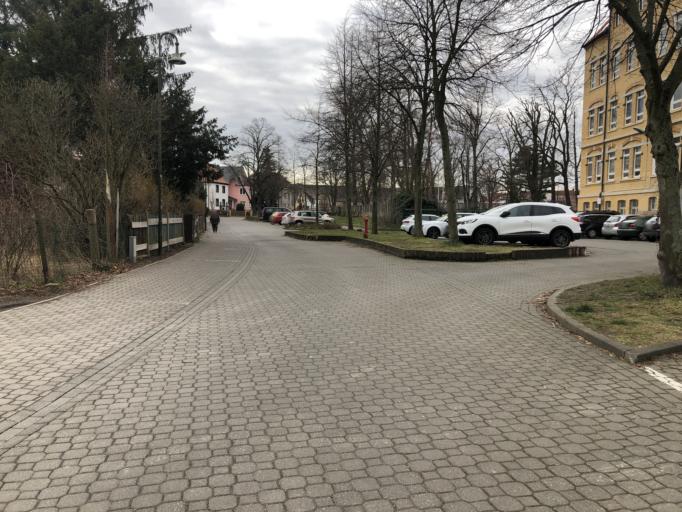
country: DE
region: Saxony
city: Grossposna
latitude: 51.2851
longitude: 12.4611
